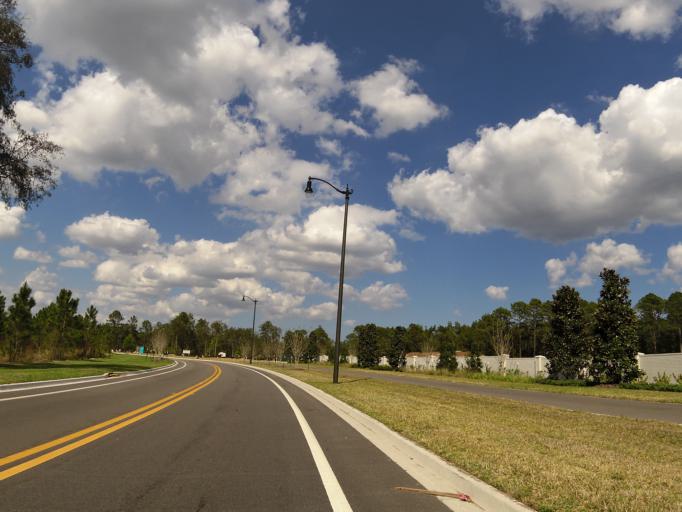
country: US
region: Florida
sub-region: Saint Johns County
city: Palm Valley
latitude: 30.1798
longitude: -81.5032
